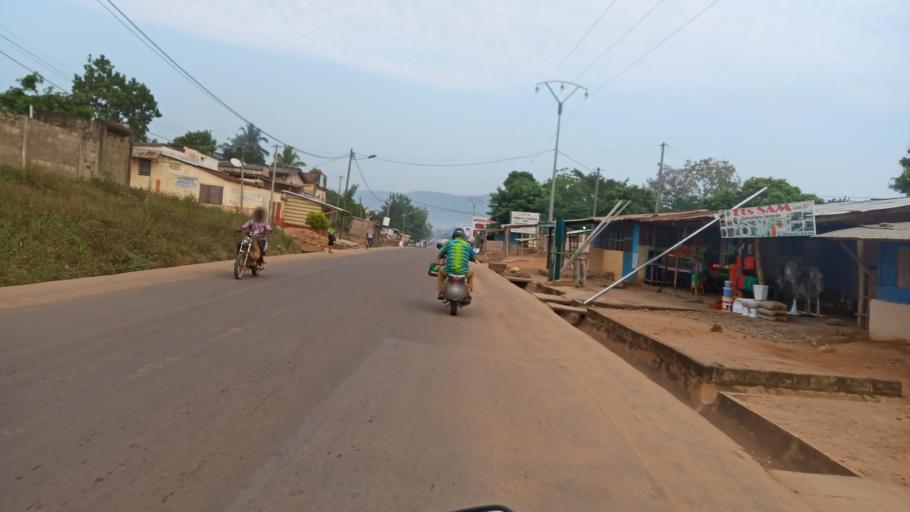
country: TG
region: Plateaux
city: Kpalime
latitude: 6.8956
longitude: 0.6382
